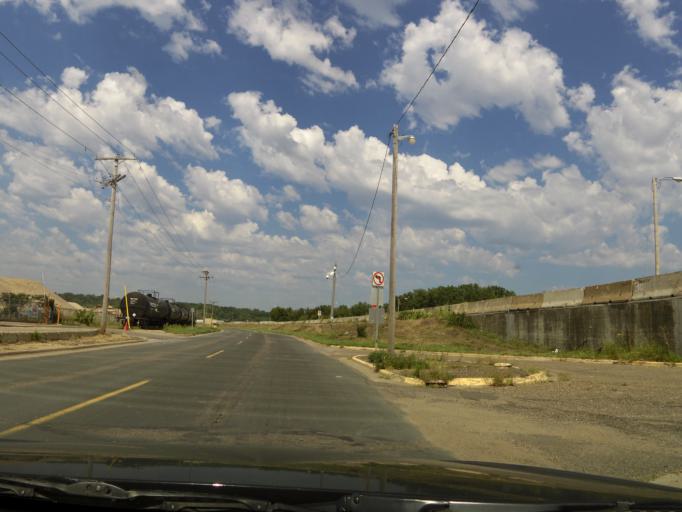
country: US
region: Minnesota
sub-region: Dakota County
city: South Saint Paul
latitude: 44.9319
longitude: -93.0461
